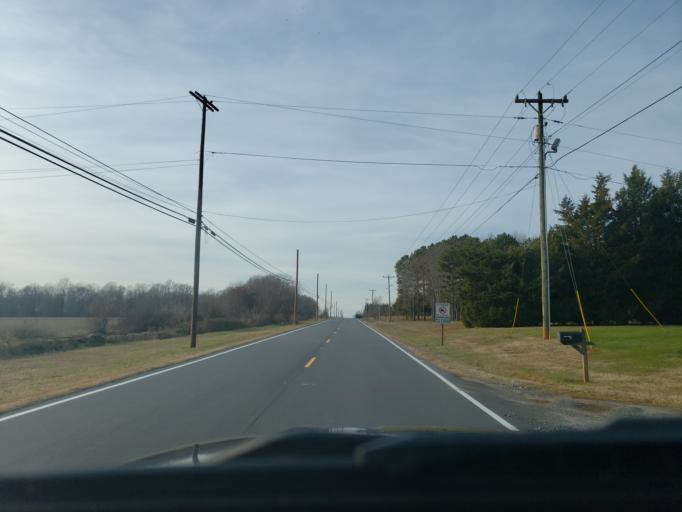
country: US
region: North Carolina
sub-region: Cleveland County
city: Boiling Springs
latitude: 35.3078
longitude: -81.7305
